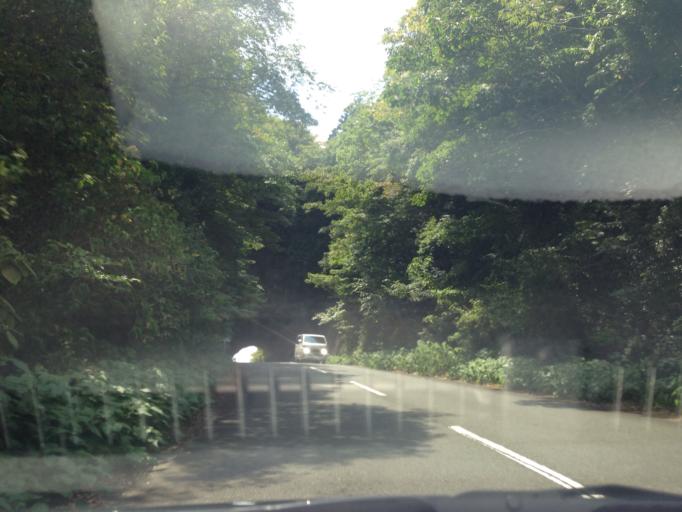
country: JP
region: Shizuoka
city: Shimoda
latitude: 34.6330
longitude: 138.8196
